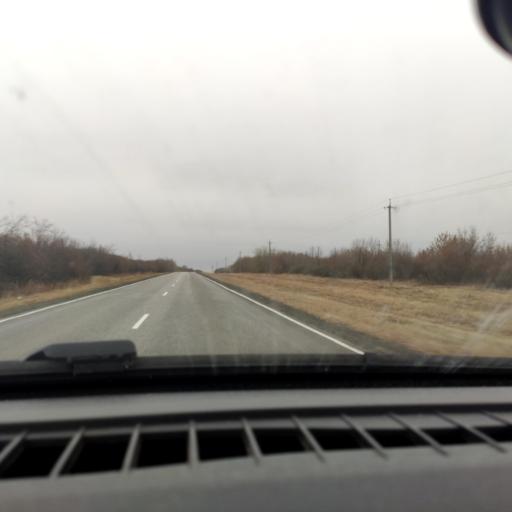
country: RU
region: Voronezj
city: Uryv-Pokrovka
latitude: 51.0943
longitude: 39.0104
